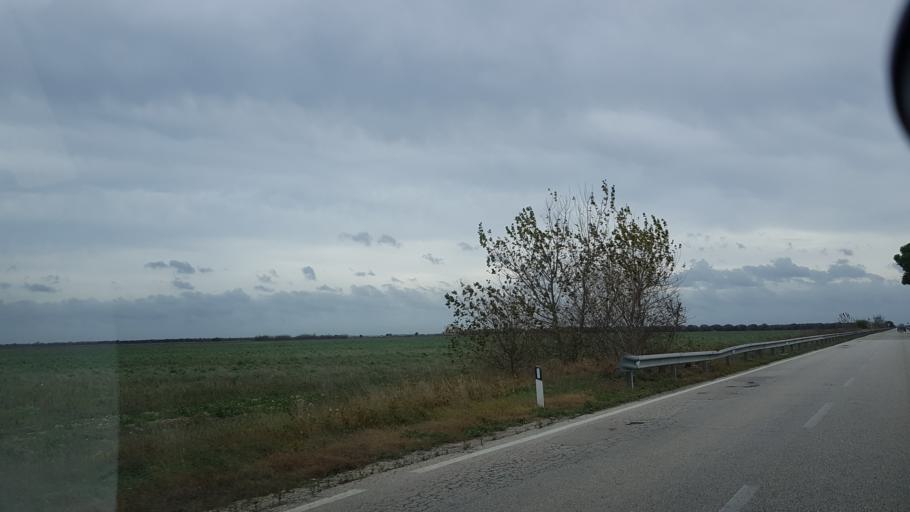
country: IT
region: Apulia
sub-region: Provincia di Brindisi
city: San Pancrazio Salentino
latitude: 40.4106
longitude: 17.8704
